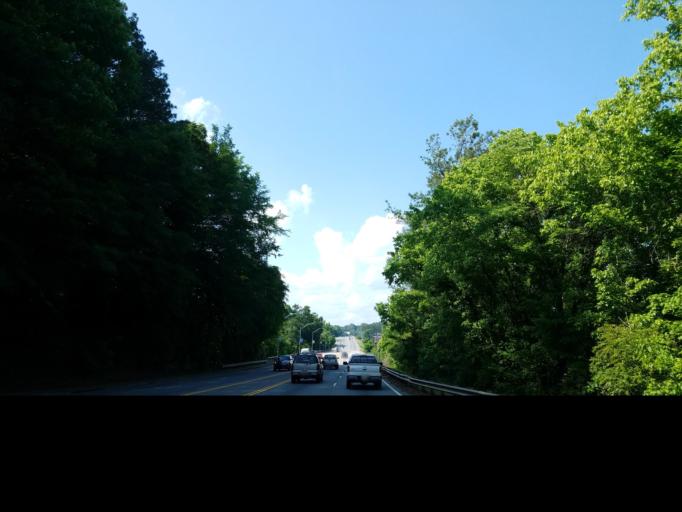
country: US
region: Georgia
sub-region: Cherokee County
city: Canton
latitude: 34.2261
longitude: -84.5002
